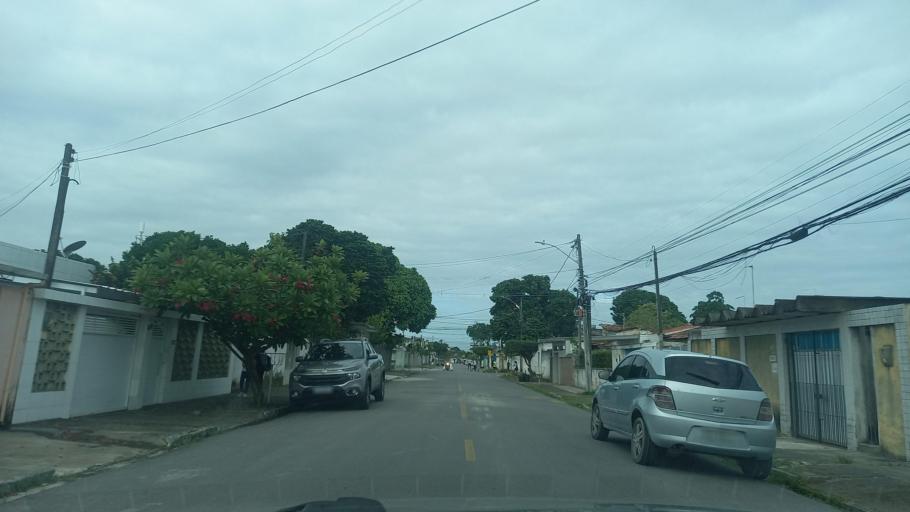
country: BR
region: Pernambuco
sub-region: Recife
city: Recife
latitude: -8.1108
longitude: -34.9211
